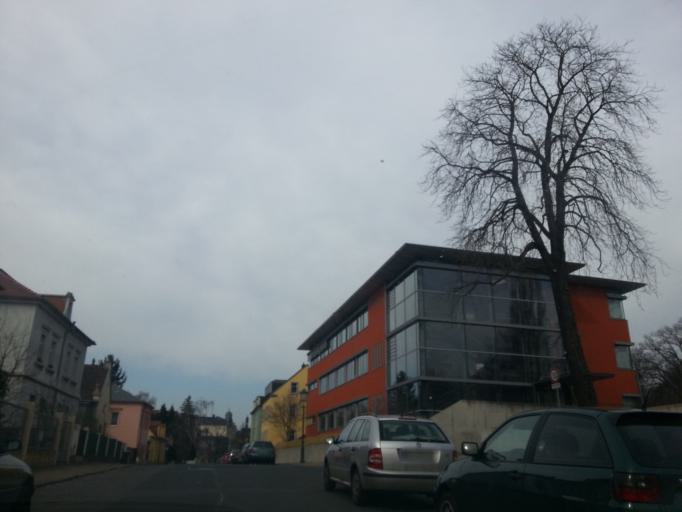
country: DE
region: Saxony
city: Albertstadt
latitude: 51.0889
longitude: 13.7339
